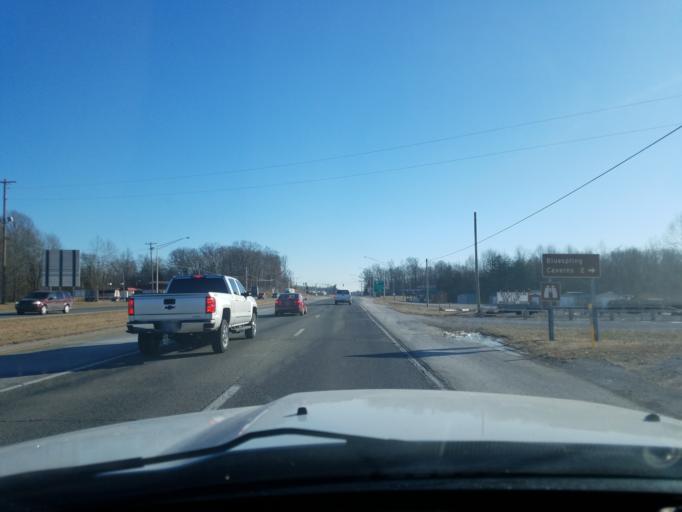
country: US
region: Indiana
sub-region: Lawrence County
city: Bedford
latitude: 38.8148
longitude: -86.5177
